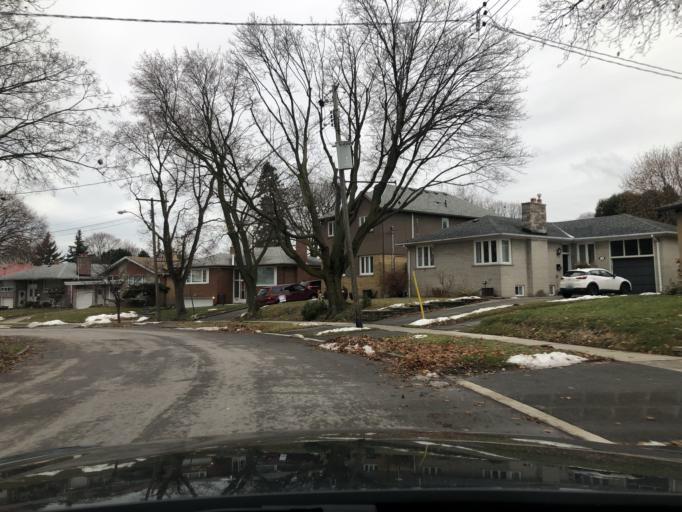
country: CA
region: Ontario
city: Etobicoke
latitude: 43.6920
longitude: -79.5333
